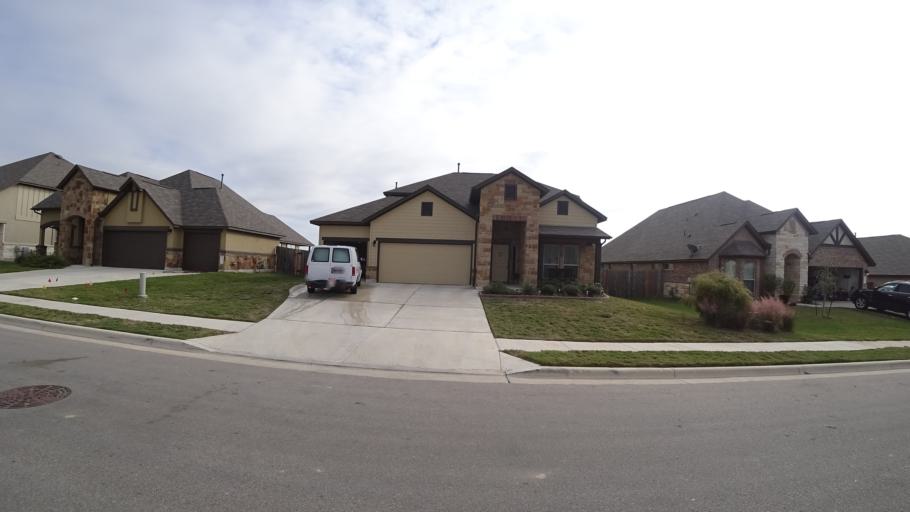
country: US
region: Texas
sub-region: Travis County
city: Manchaca
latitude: 30.1341
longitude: -97.8477
